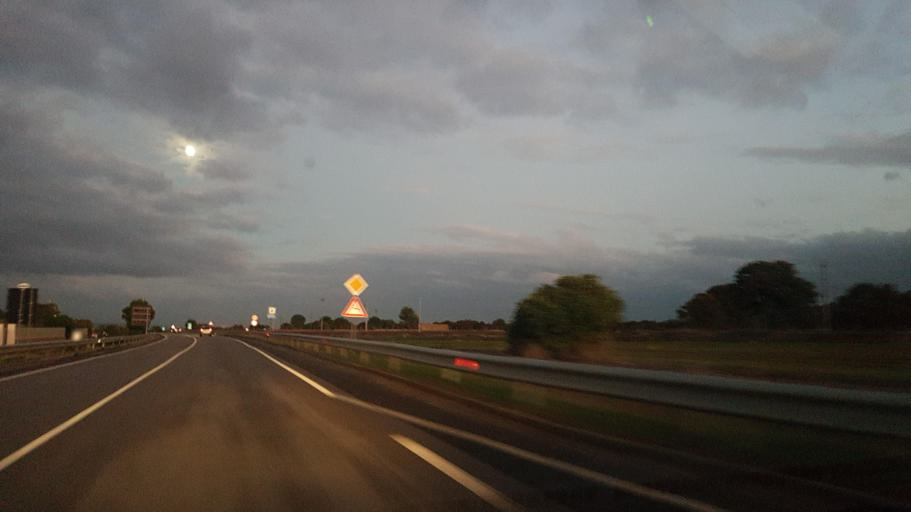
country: IT
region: Apulia
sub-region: Provincia di Taranto
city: Laterza
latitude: 40.6488
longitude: 16.8262
